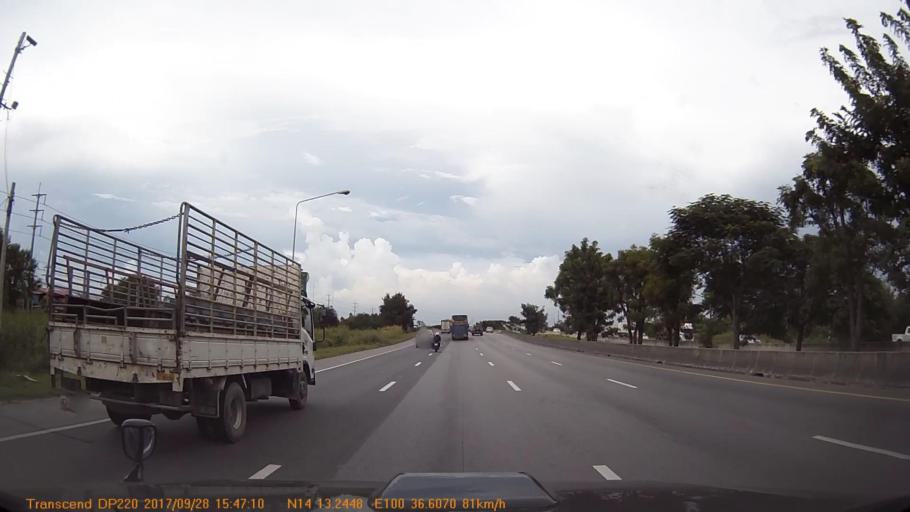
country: TH
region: Phra Nakhon Si Ayutthaya
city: Bang Pa-in
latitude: 14.2208
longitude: 100.6101
